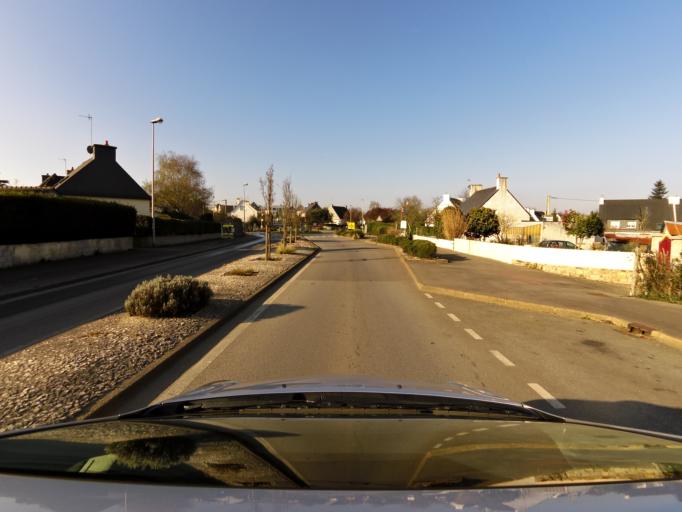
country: FR
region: Brittany
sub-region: Departement du Morbihan
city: Ploemeur
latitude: 47.7406
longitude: -3.4267
